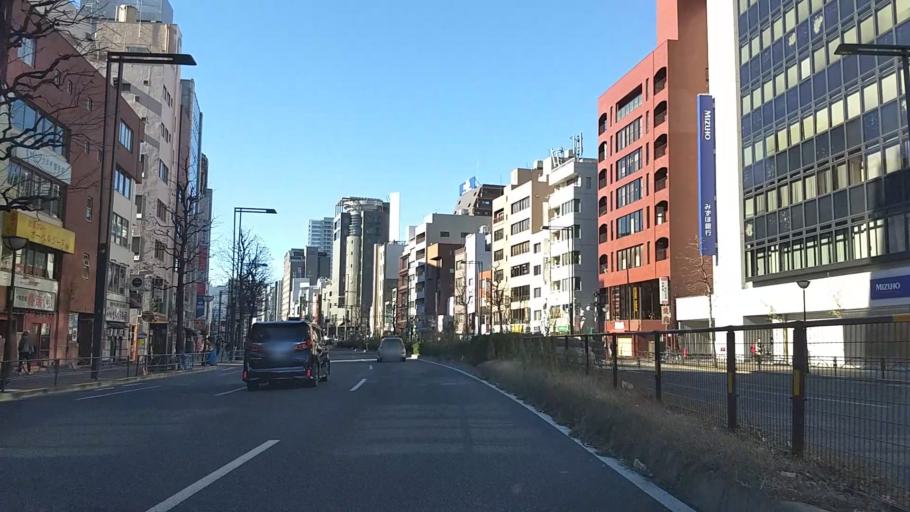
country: JP
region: Tokyo
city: Tokyo
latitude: 35.6880
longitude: 139.7227
